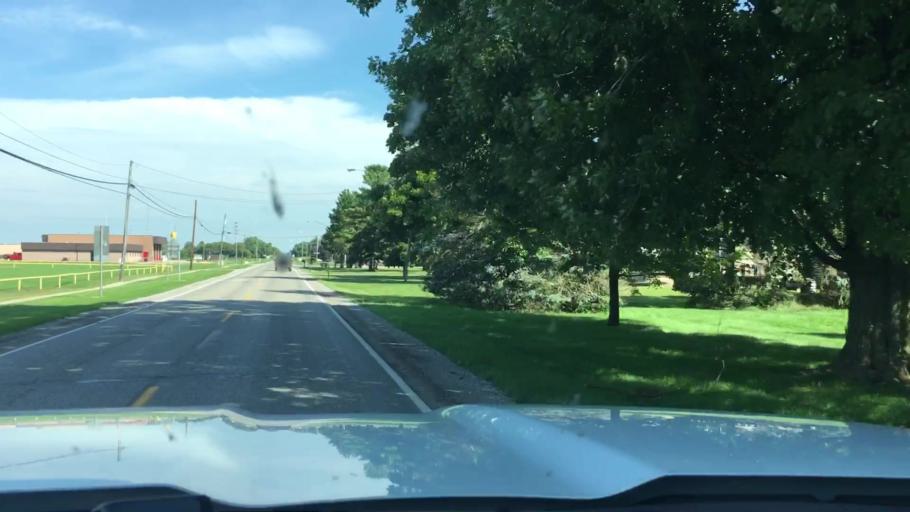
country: US
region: Michigan
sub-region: Saginaw County
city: Hemlock
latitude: 43.4212
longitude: -84.2298
